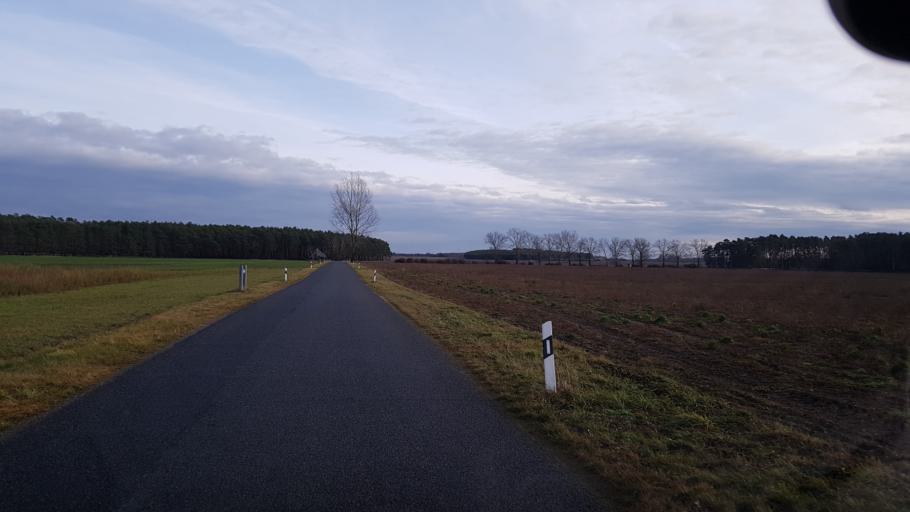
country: DE
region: Brandenburg
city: Bronkow
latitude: 51.6632
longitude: 13.8734
